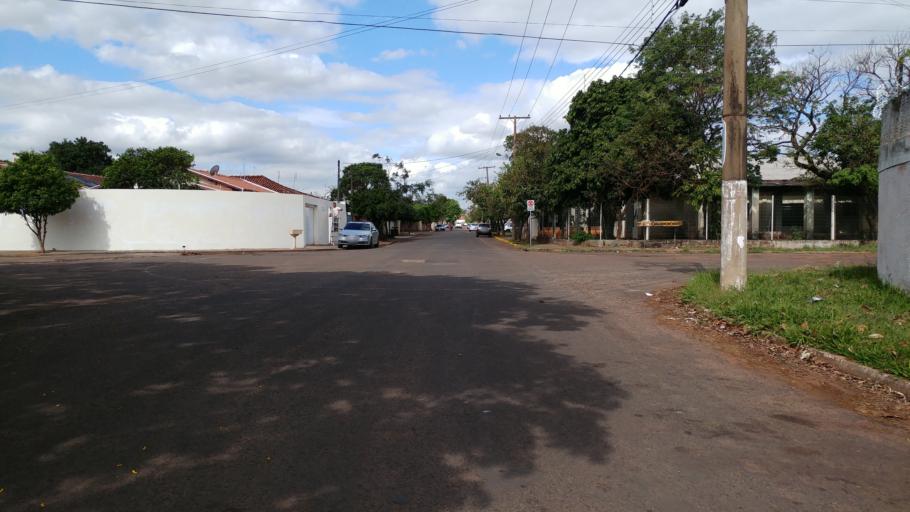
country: BR
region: Sao Paulo
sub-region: Paraguacu Paulista
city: Paraguacu Paulista
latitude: -22.4166
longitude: -50.5930
